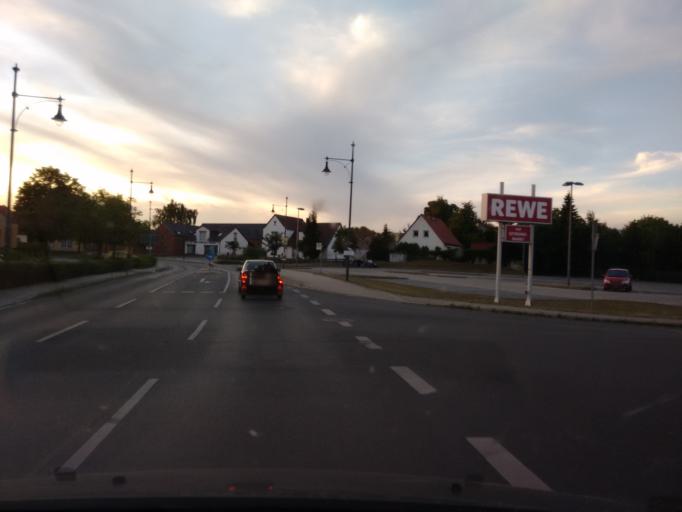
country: DE
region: Brandenburg
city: Beeskow
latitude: 52.1727
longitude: 14.2518
